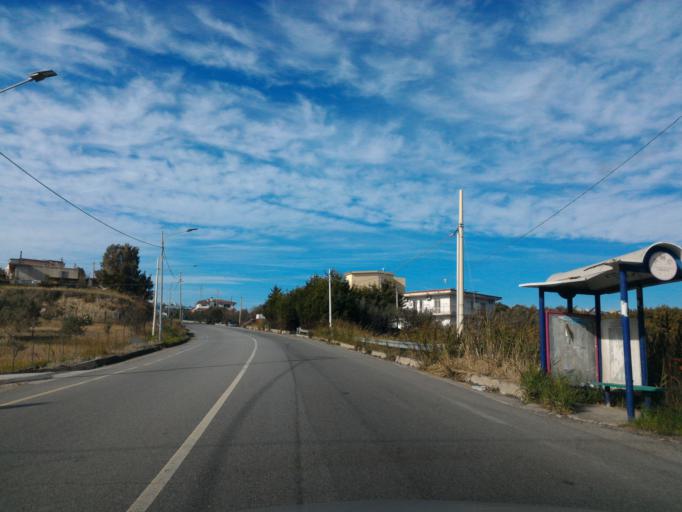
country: IT
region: Calabria
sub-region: Provincia di Catanzaro
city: Cava-Cuculera Nobile
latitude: 38.9046
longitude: 16.6165
